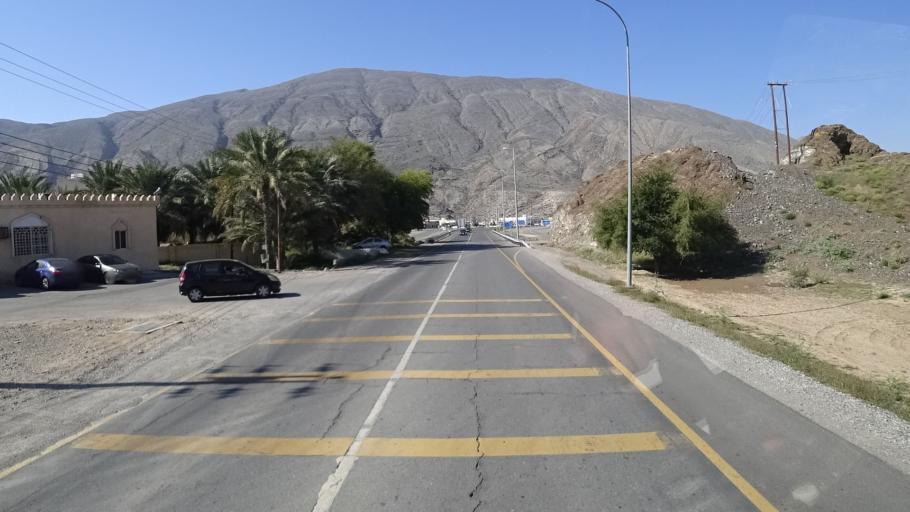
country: OM
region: Al Batinah
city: Bayt al `Awabi
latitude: 23.3125
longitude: 57.5246
